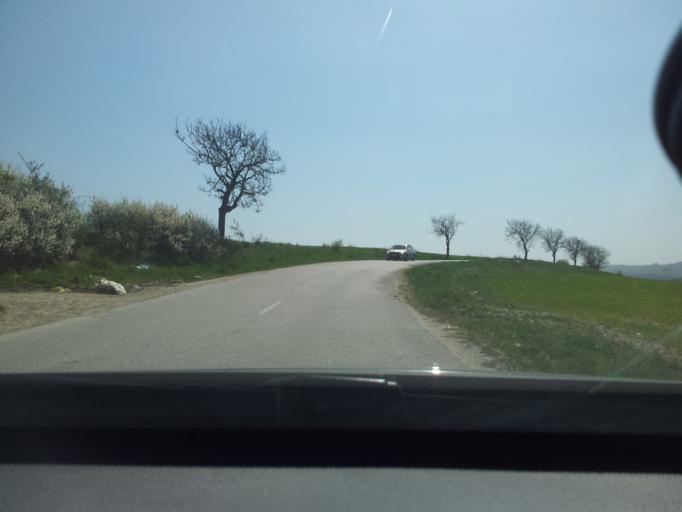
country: SK
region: Nitriansky
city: Partizanske
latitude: 48.5895
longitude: 18.3117
